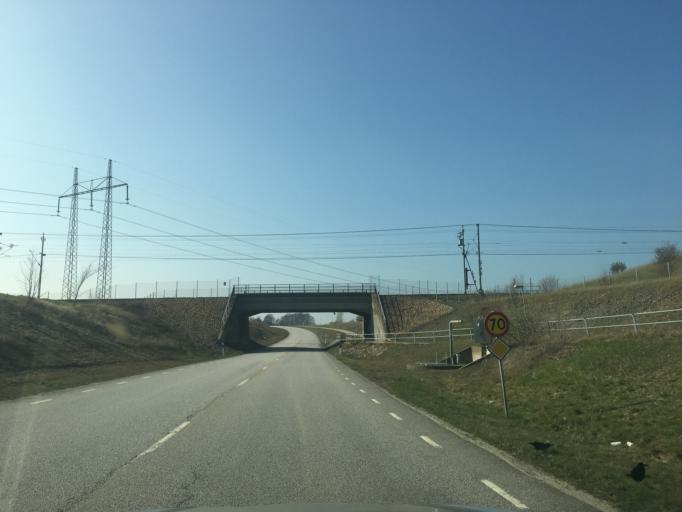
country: SE
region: Skane
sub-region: Staffanstorps Kommun
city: Hjaerup
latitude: 55.6686
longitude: 13.1290
